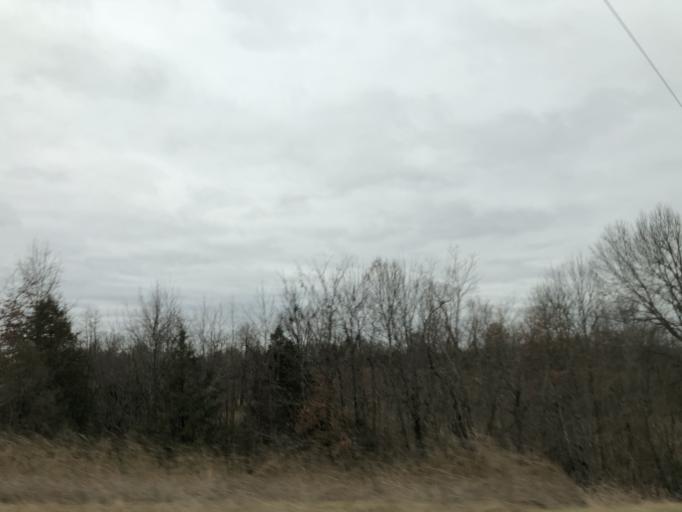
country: US
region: Illinois
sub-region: Johnson County
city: Vienna
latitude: 37.4094
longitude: -88.8668
